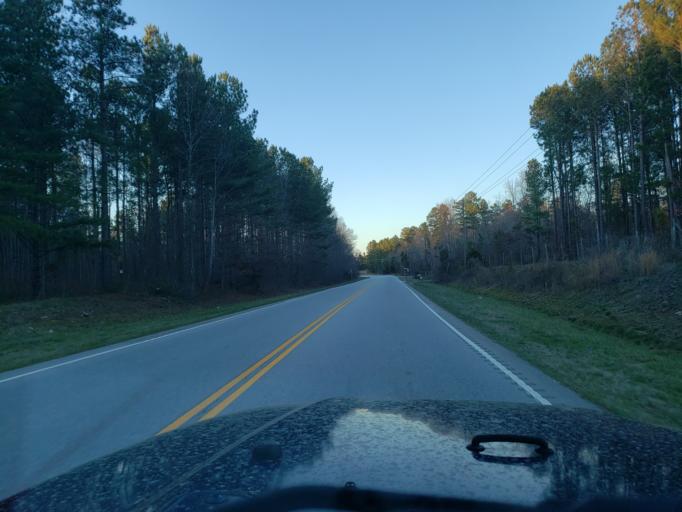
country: US
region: South Carolina
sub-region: York County
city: Clover
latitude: 35.1377
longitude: -81.3130
